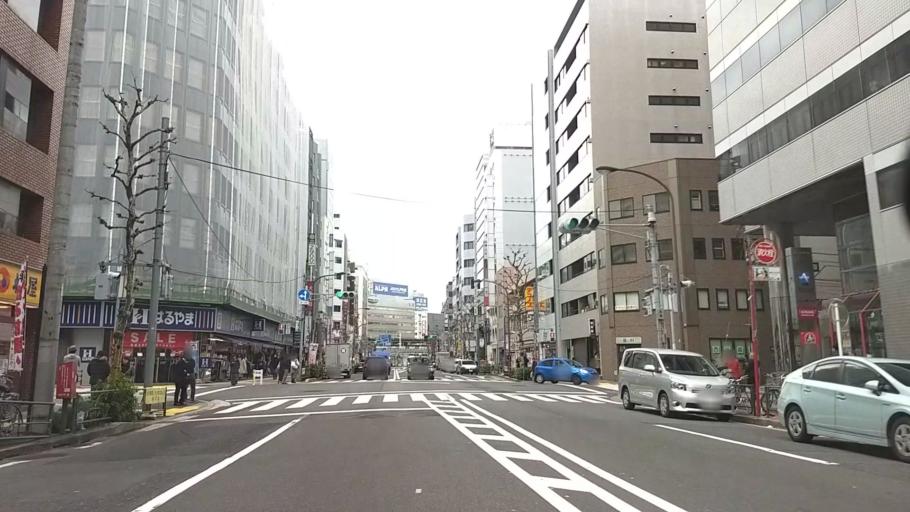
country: JP
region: Tokyo
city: Tokyo
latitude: 35.6256
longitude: 139.7273
